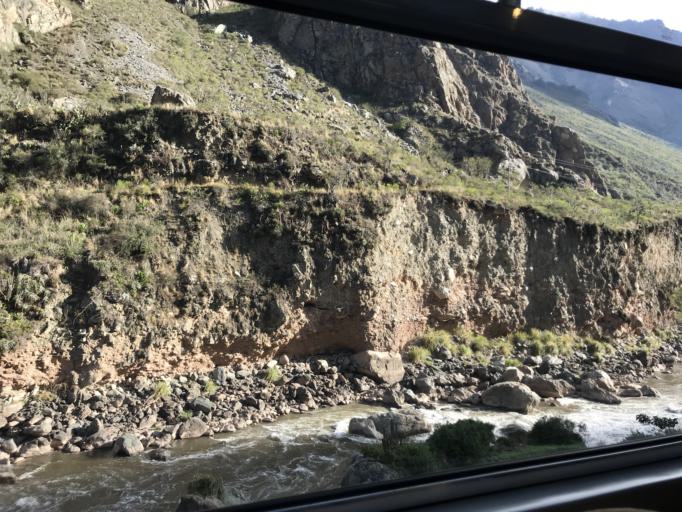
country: PE
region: Cusco
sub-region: Provincia de Urubamba
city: Ollantaytambo
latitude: -13.2170
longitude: -72.3860
